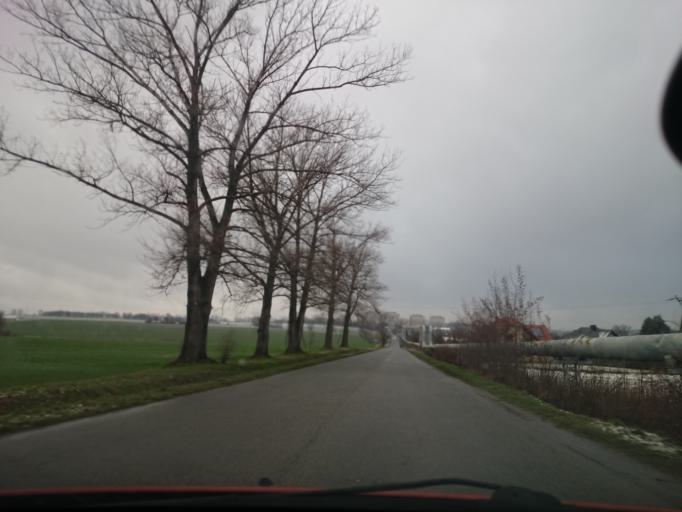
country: PL
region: Lower Silesian Voivodeship
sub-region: Powiat klodzki
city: Klodzko
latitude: 50.4216
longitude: 16.6371
